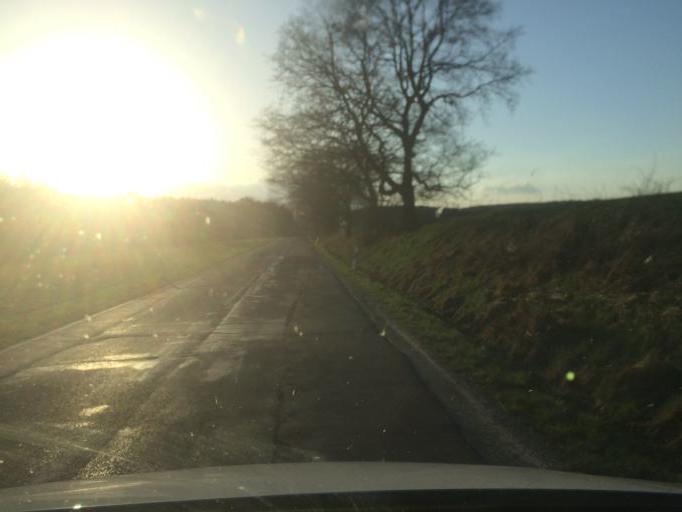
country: DE
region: Thuringia
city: Bischofferode
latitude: 51.5326
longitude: 10.4805
